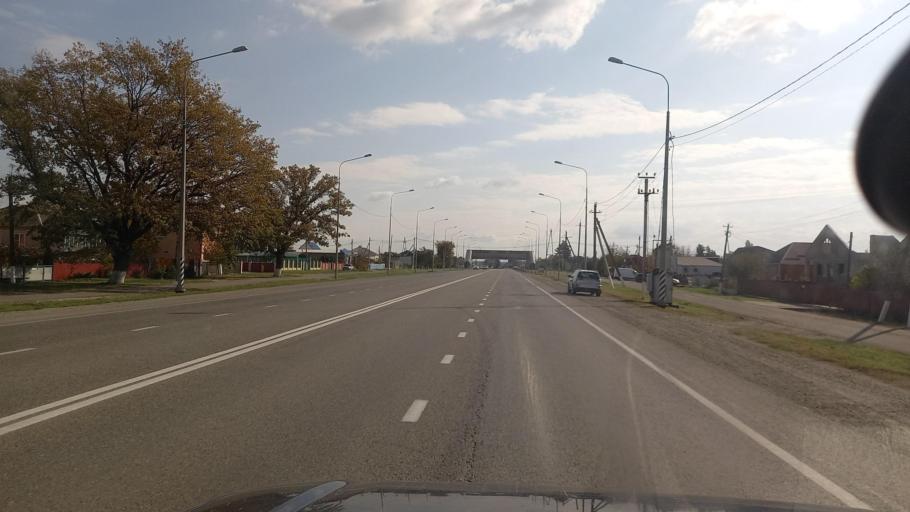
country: RU
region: Krasnodarskiy
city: Novoukrainskiy
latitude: 44.8973
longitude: 38.0464
